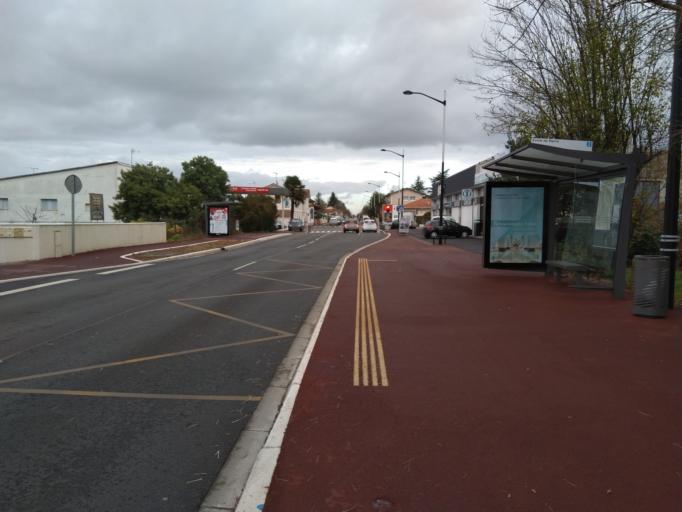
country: FR
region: Aquitaine
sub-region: Departement des Landes
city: Dax
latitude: 43.6982
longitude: -1.0662
